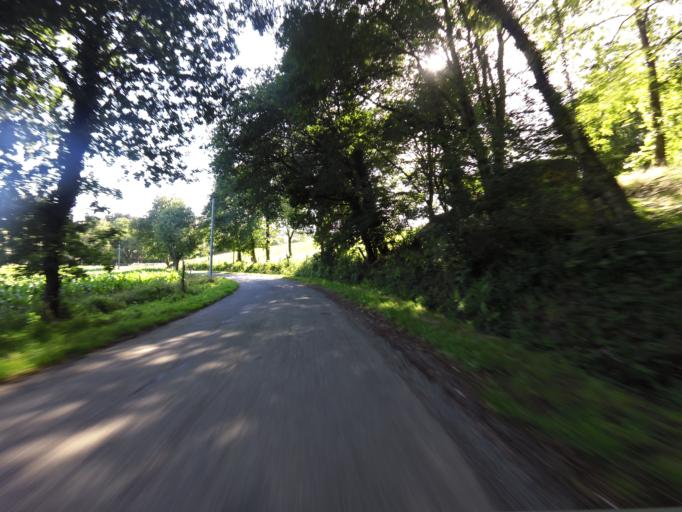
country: FR
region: Brittany
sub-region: Departement du Morbihan
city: Limerzel
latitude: 47.6285
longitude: -2.3569
